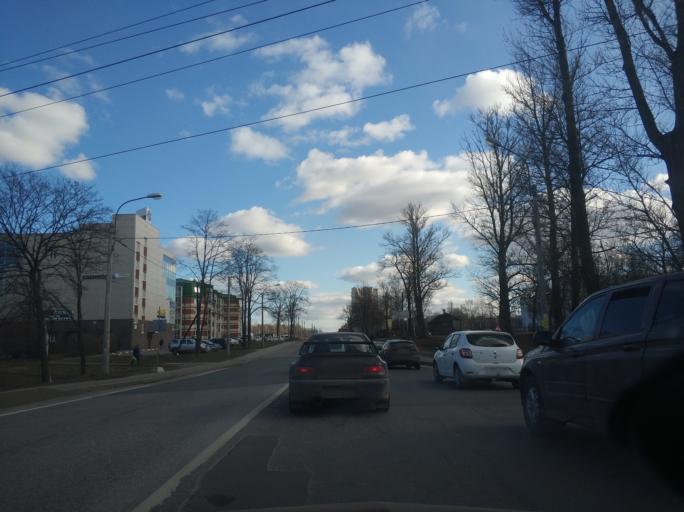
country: RU
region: St.-Petersburg
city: Krasnogvargeisky
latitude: 59.9656
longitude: 30.4848
